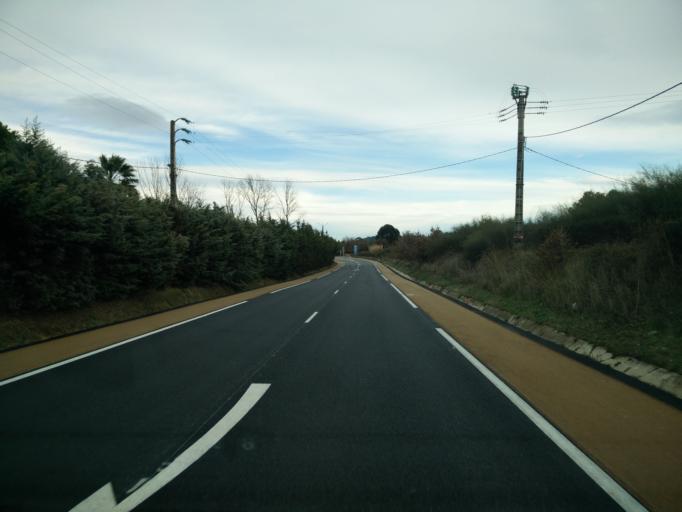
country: FR
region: Provence-Alpes-Cote d'Azur
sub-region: Departement du Var
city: Puget-sur-Argens
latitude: 43.4266
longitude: 6.6722
